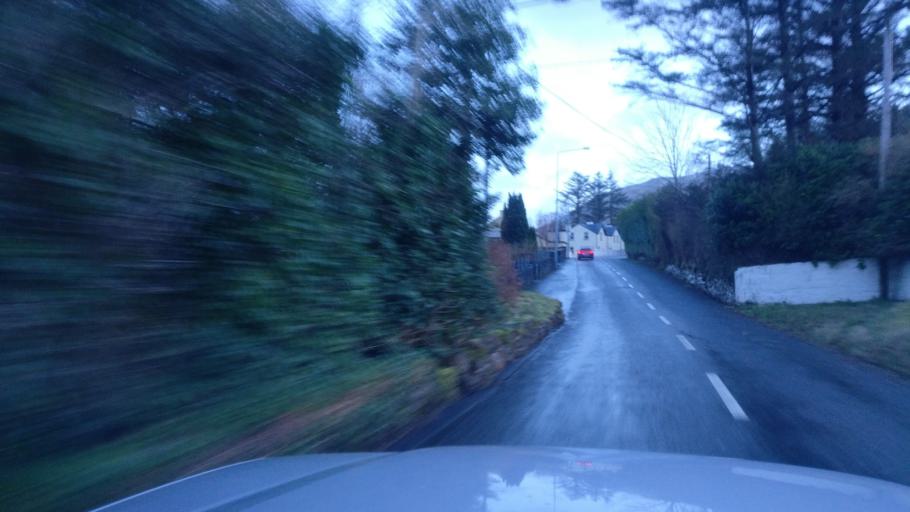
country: IE
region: Connaught
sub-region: Maigh Eo
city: Westport
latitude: 53.5950
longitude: -9.6923
